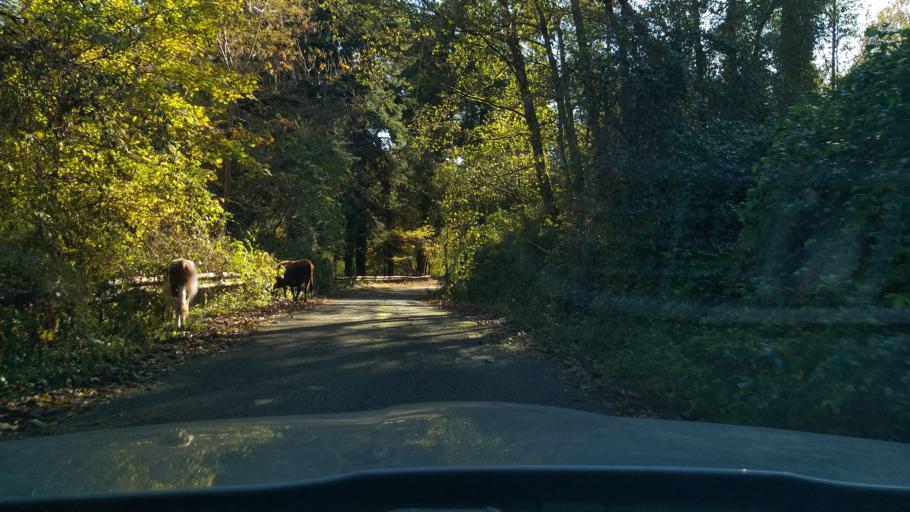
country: GE
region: Abkhazia
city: Bich'vinta
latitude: 43.1825
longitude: 40.4547
